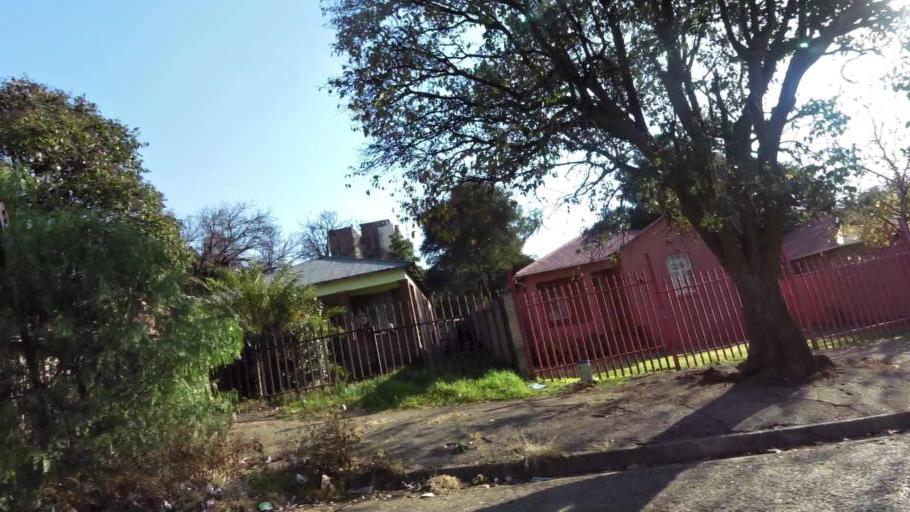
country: ZA
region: Gauteng
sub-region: City of Johannesburg Metropolitan Municipality
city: Johannesburg
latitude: -26.1901
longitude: 28.0154
